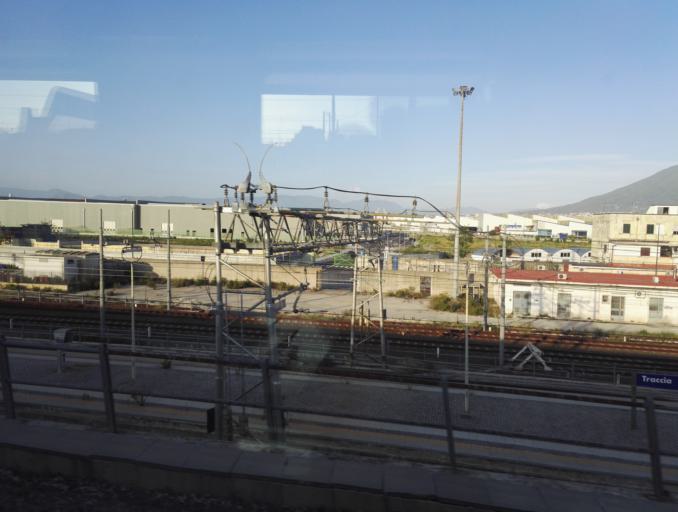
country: IT
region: Campania
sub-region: Provincia di Napoli
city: Arpino
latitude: 40.8589
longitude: 14.2971
